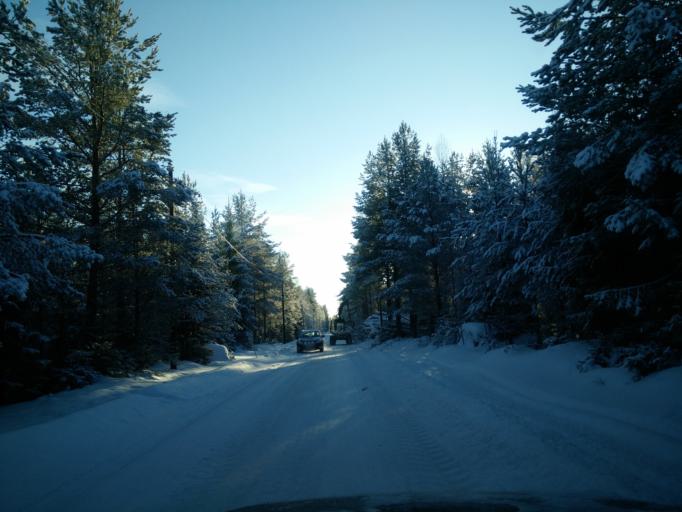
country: SE
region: Vaesternorrland
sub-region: Sundsvalls Kommun
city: Njurundabommen
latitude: 62.2151
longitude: 17.4936
